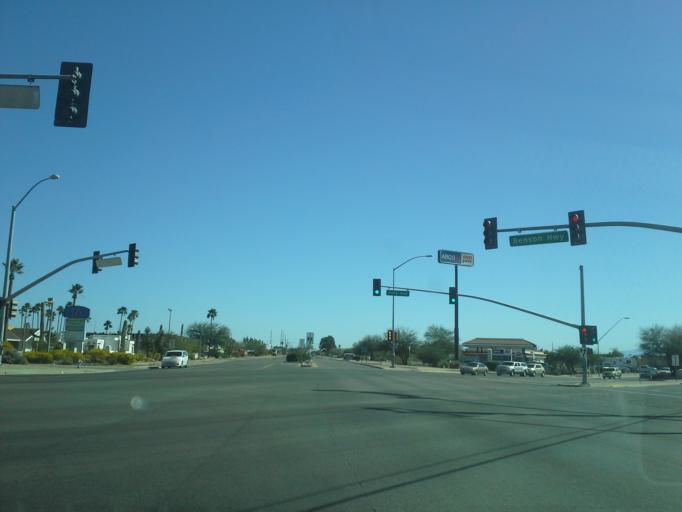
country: US
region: Arizona
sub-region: Pima County
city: South Tucson
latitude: 32.1819
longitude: -110.9564
